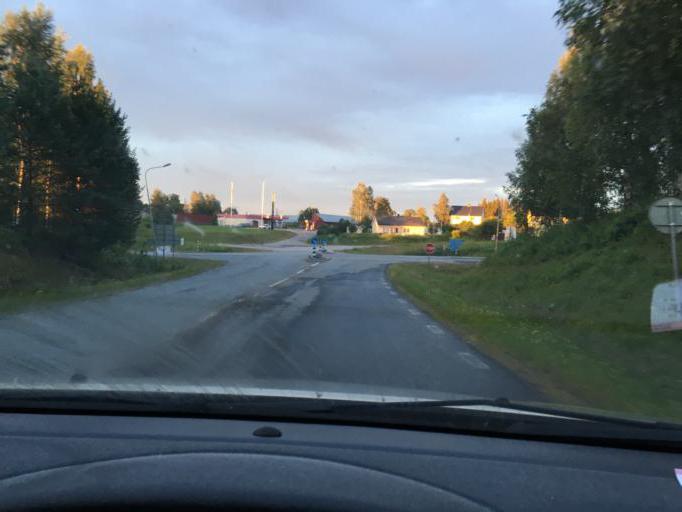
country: SE
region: Norrbotten
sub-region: Kalix Kommun
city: Toere
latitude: 66.0696
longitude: 22.7050
